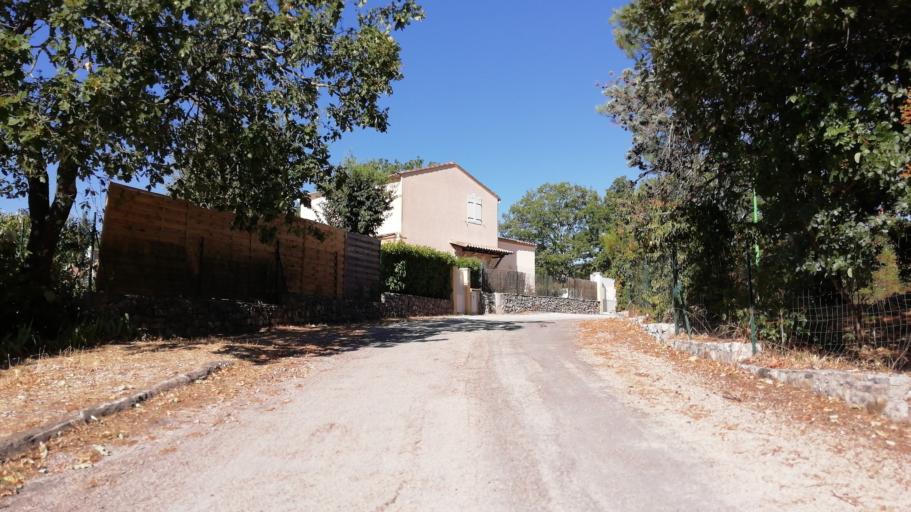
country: FR
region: Languedoc-Roussillon
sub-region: Departement de l'Herault
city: Saint-Martin-de-Londres
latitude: 43.7889
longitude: 3.7261
